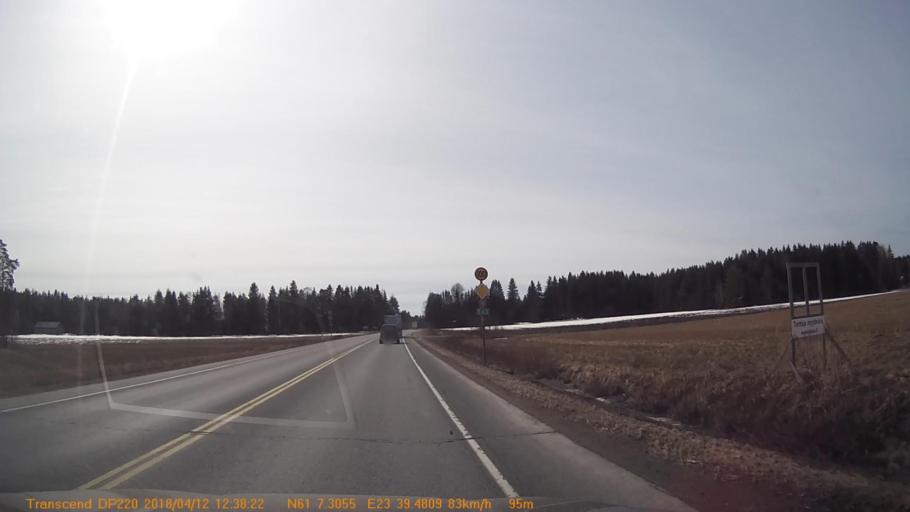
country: FI
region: Pirkanmaa
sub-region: Etelae-Pirkanmaa
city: Kylmaekoski
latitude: 61.1219
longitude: 23.6581
